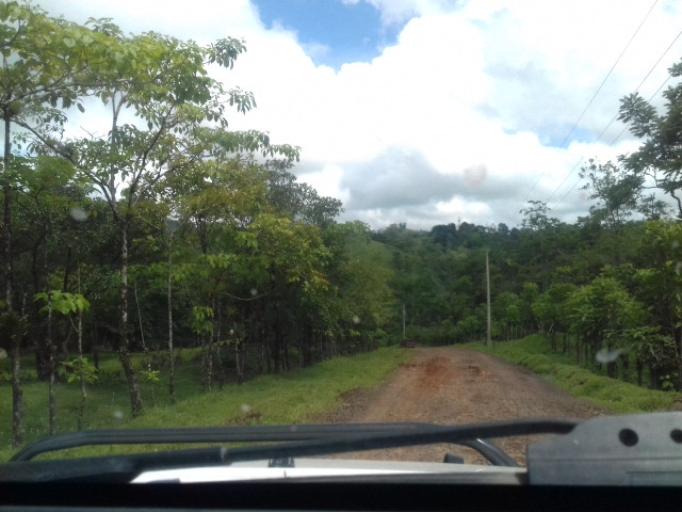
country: NI
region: Matagalpa
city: Rio Blanco
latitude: 13.0014
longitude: -85.1993
